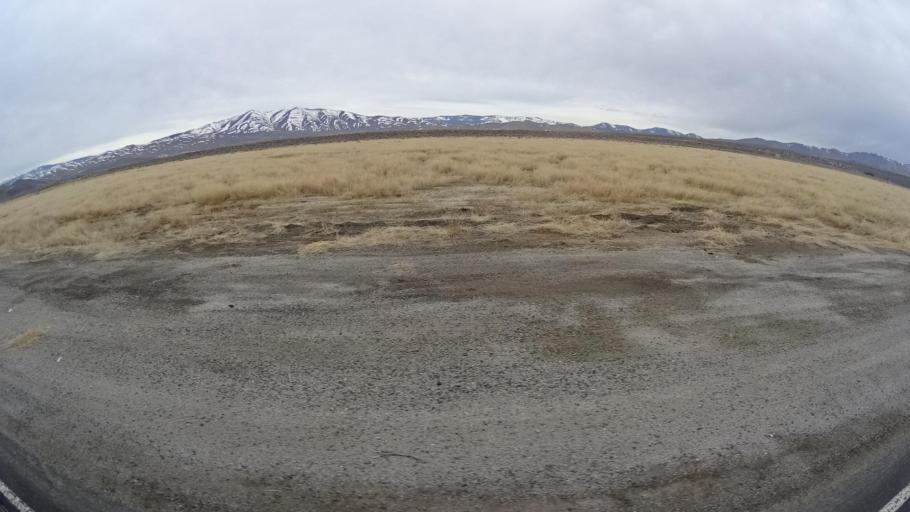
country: US
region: Nevada
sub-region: Washoe County
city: Lemmon Valley
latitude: 39.6624
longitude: -119.8289
